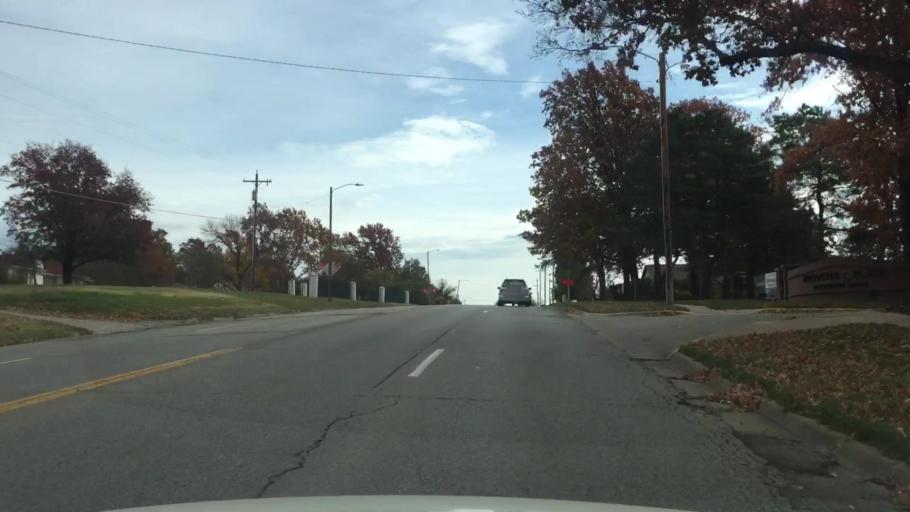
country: US
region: Kansas
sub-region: Shawnee County
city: Topeka
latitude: 39.0151
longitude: -95.6929
